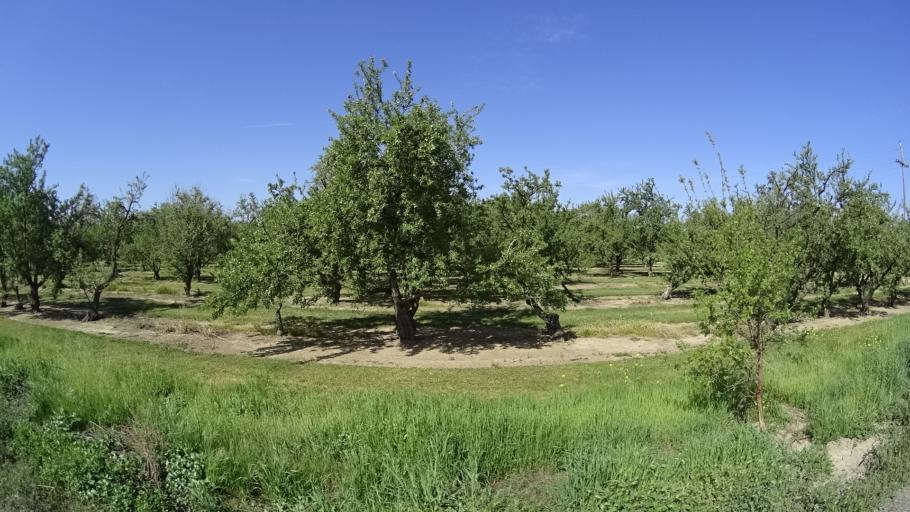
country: US
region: California
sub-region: Glenn County
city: Hamilton City
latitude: 39.6256
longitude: -122.0181
